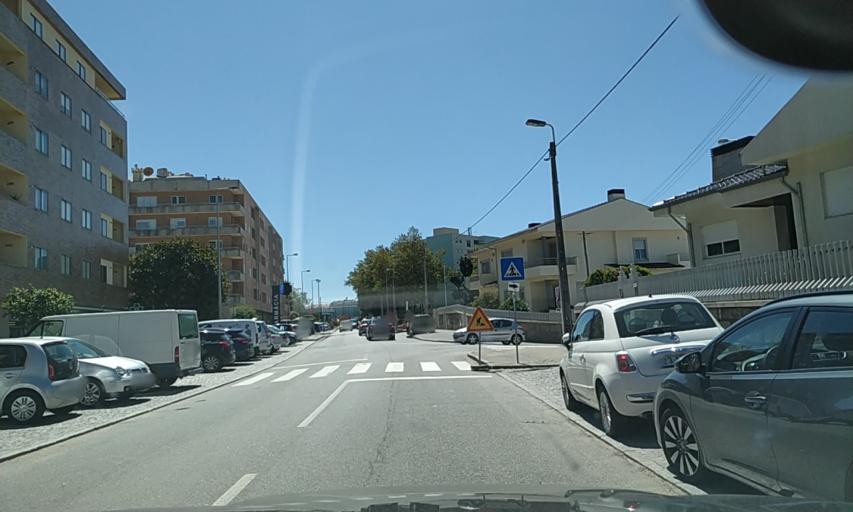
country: PT
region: Porto
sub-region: Vila Nova de Gaia
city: Canidelo
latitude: 41.1359
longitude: -8.6450
